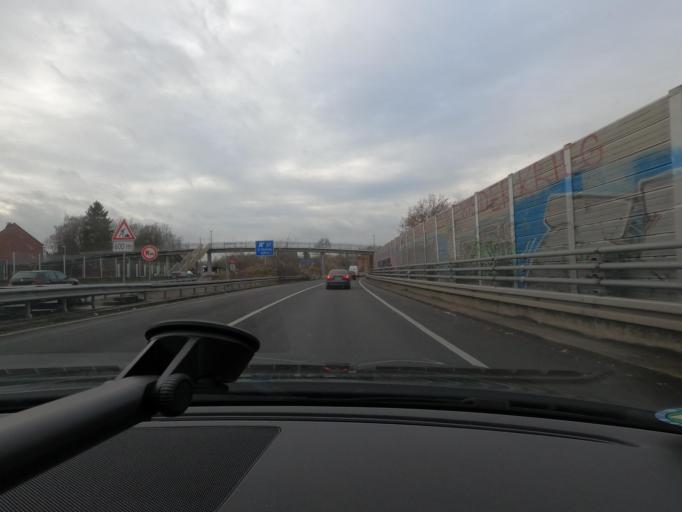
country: DE
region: North Rhine-Westphalia
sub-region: Regierungsbezirk Dusseldorf
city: Essen
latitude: 51.4557
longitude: 7.0441
